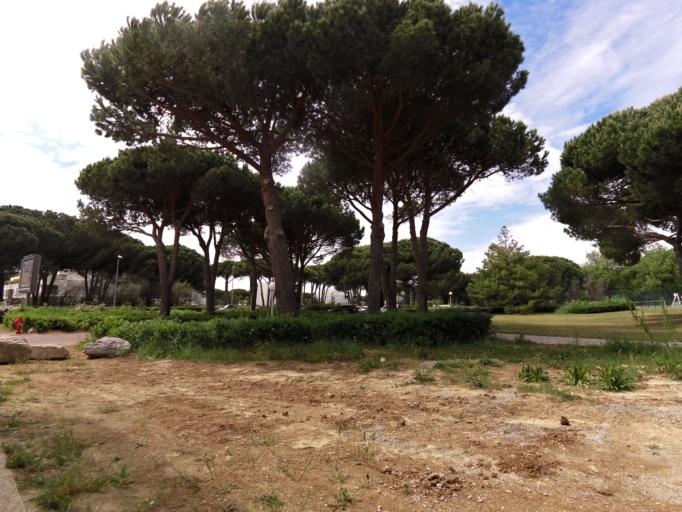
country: FR
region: Languedoc-Roussillon
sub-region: Departement de l'Herault
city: La Grande-Motte
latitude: 43.5592
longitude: 4.0989
